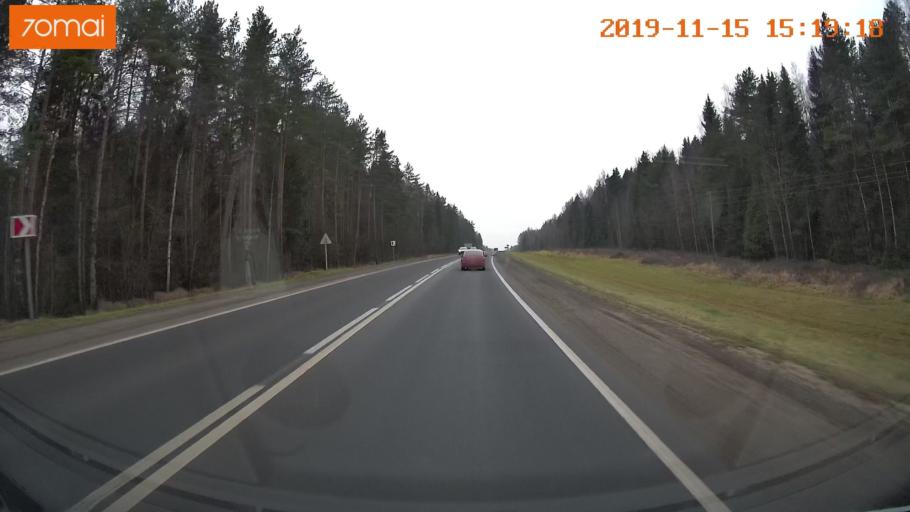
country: RU
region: Jaroslavl
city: Danilov
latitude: 58.2358
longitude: 40.1798
